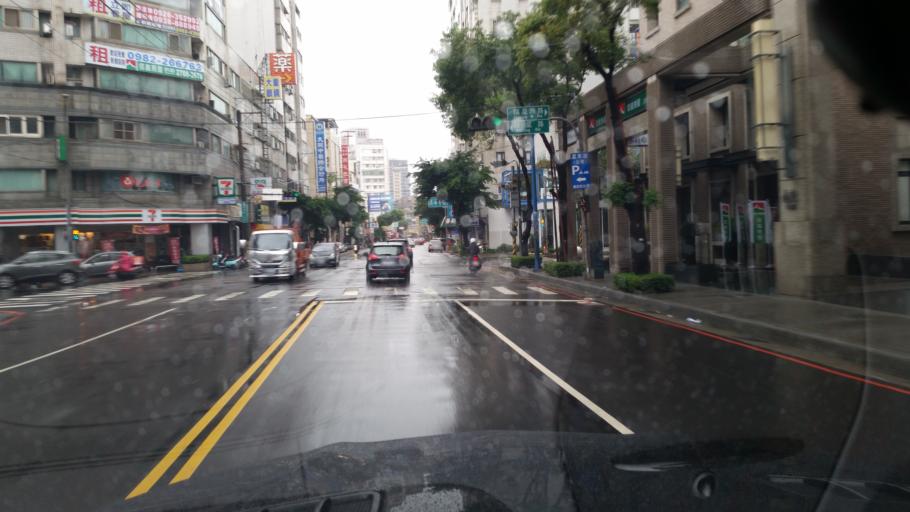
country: TW
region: Taiwan
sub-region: Taichung City
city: Taichung
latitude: 24.1826
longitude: 120.6390
